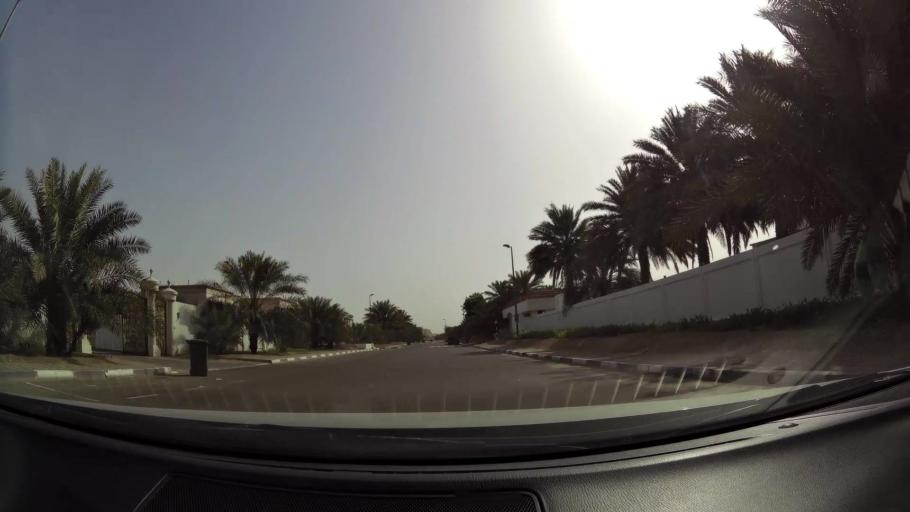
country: AE
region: Abu Dhabi
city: Al Ain
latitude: 24.1443
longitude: 55.6979
